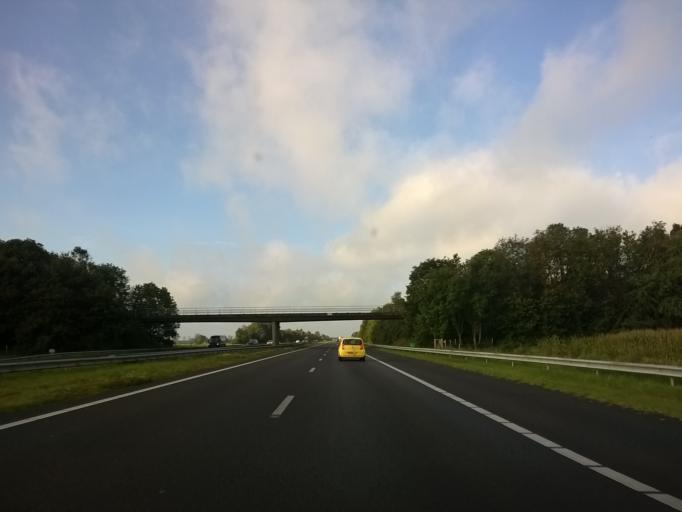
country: NL
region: Friesland
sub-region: Gemeente Achtkarspelen
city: Surhuisterveen
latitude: 53.1394
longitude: 6.2184
